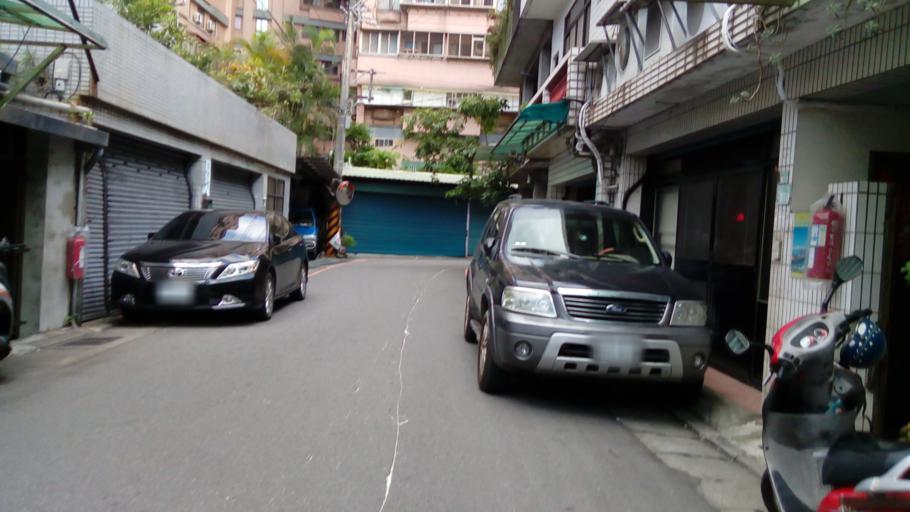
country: TW
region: Taipei
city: Taipei
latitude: 25.1793
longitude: 121.4450
